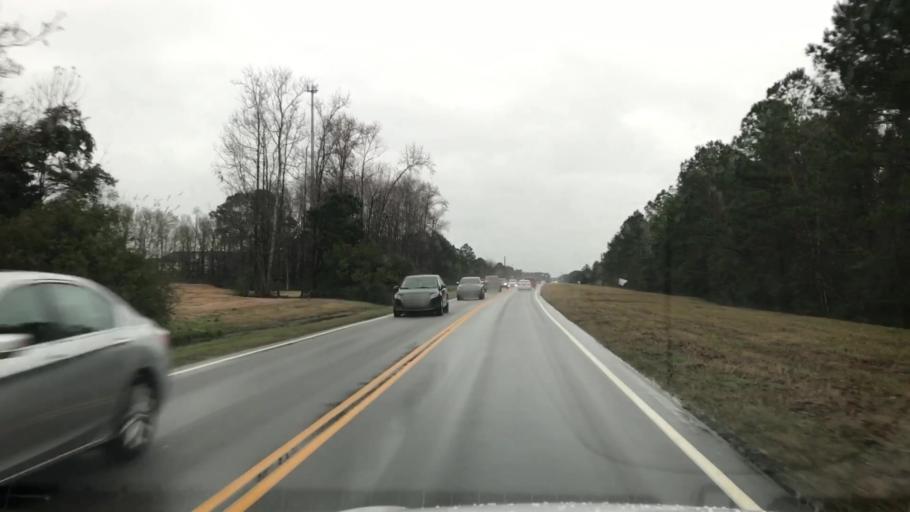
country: US
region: South Carolina
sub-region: Horry County
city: Myrtle Beach
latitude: 33.7338
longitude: -78.9029
